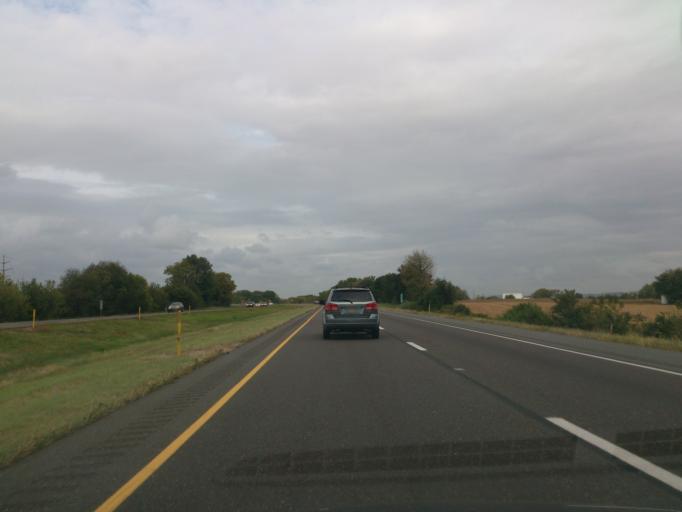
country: US
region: Pennsylvania
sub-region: Lancaster County
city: Ephrata
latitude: 40.1532
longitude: -76.1603
